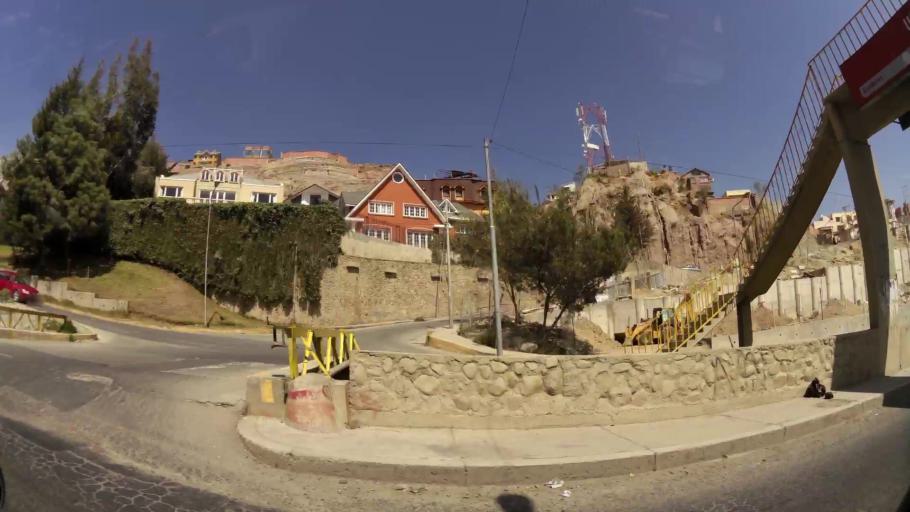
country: BO
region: La Paz
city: La Paz
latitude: -16.5457
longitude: -68.0850
